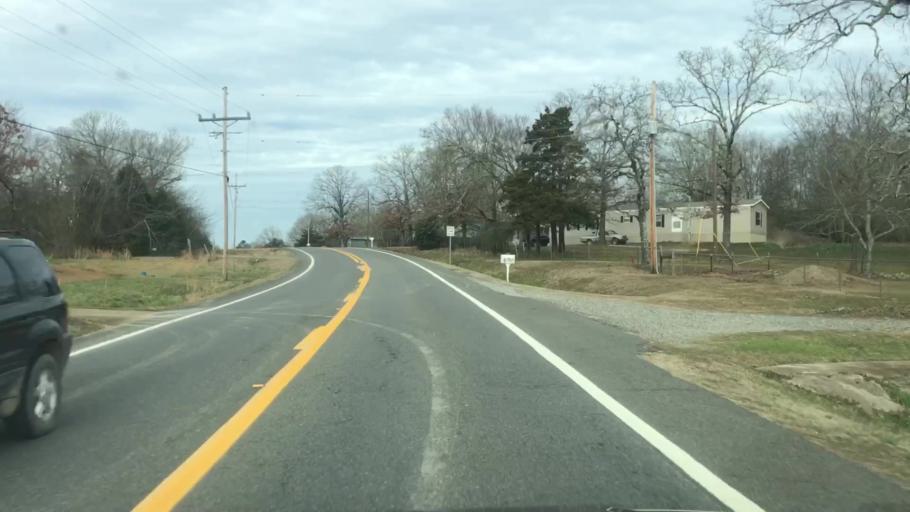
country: US
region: Arkansas
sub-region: Montgomery County
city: Mount Ida
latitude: 34.6236
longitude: -93.7266
